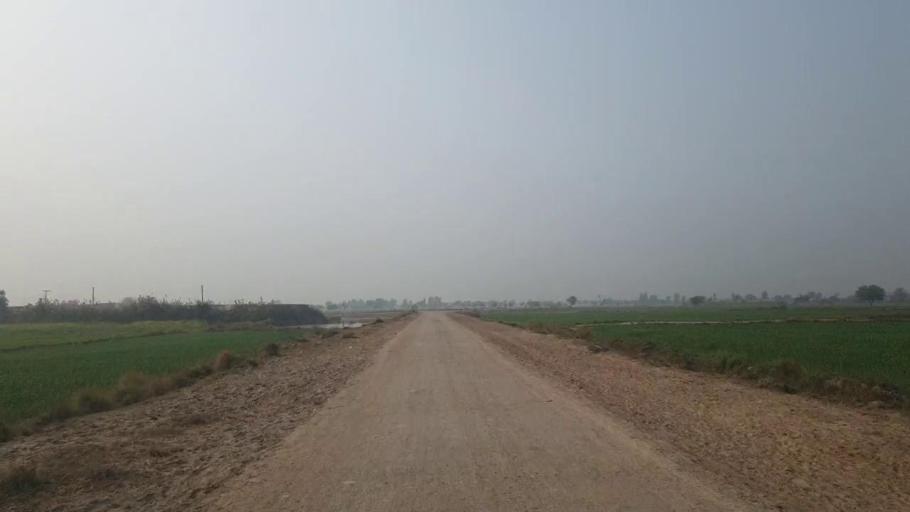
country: PK
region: Sindh
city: Shahdadpur
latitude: 25.8379
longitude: 68.5831
